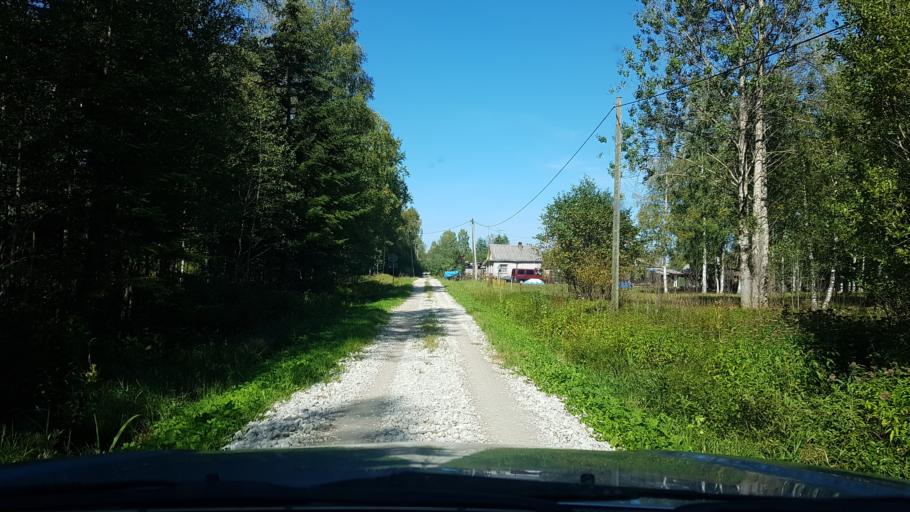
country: EE
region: Ida-Virumaa
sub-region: Sillamaee linn
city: Sillamae
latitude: 59.3157
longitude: 27.7868
